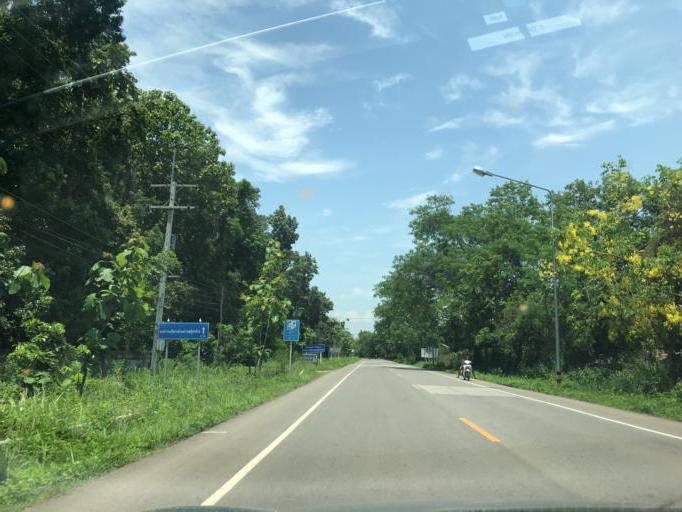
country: TH
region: Phayao
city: Phu Sang
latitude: 19.5804
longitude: 100.3026
